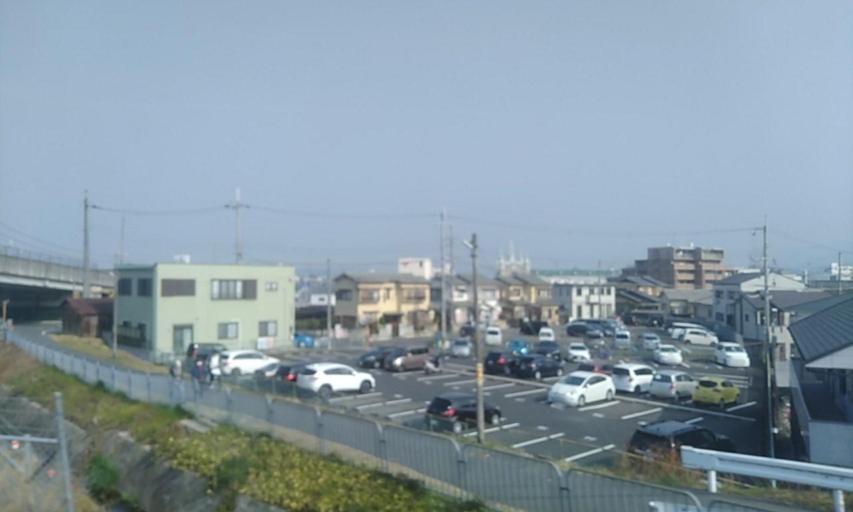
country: JP
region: Kyoto
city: Uji
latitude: 34.8889
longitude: 135.7929
